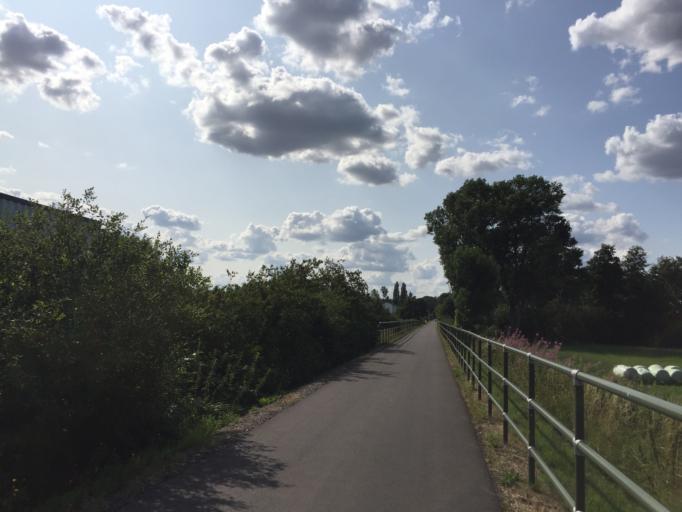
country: DE
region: Hesse
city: Schwalmstadt
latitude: 50.9054
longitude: 9.2210
